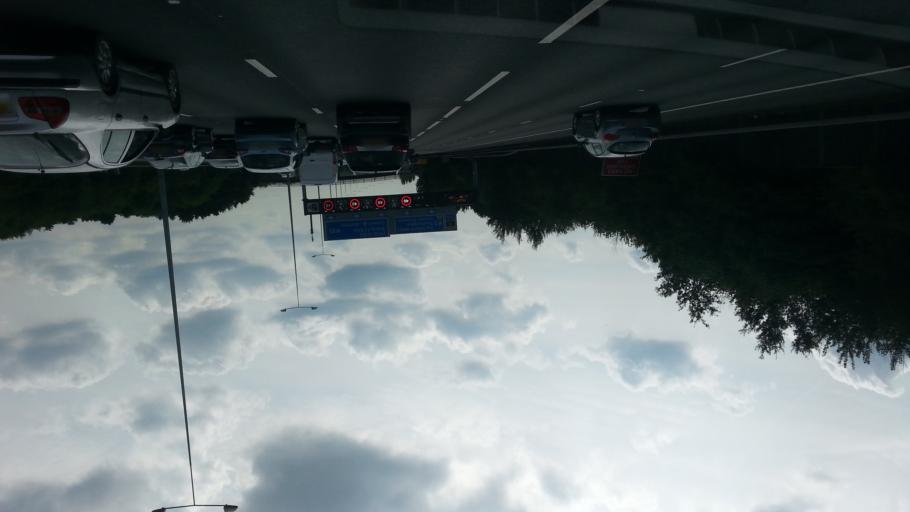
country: GB
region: England
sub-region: Surrey
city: Egham
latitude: 51.4164
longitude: -0.5397
